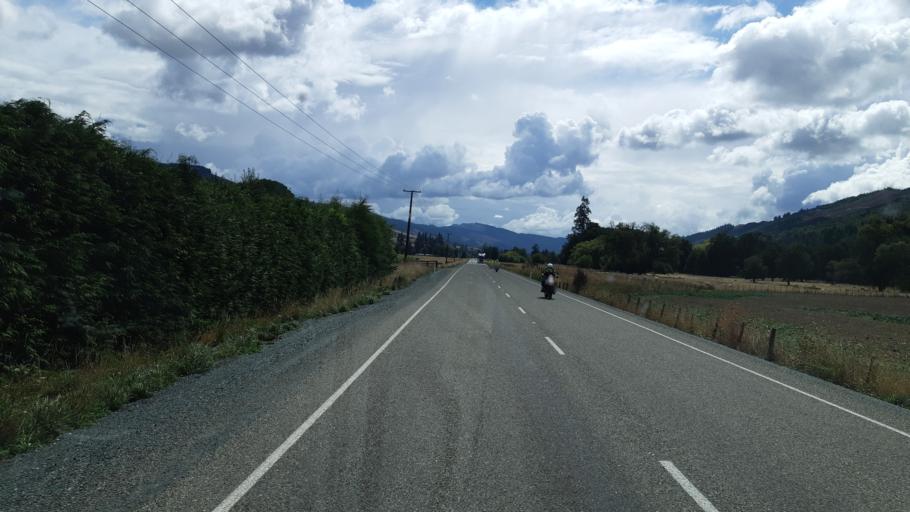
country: NZ
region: Tasman
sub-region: Tasman District
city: Wakefield
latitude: -41.5284
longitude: 172.7958
